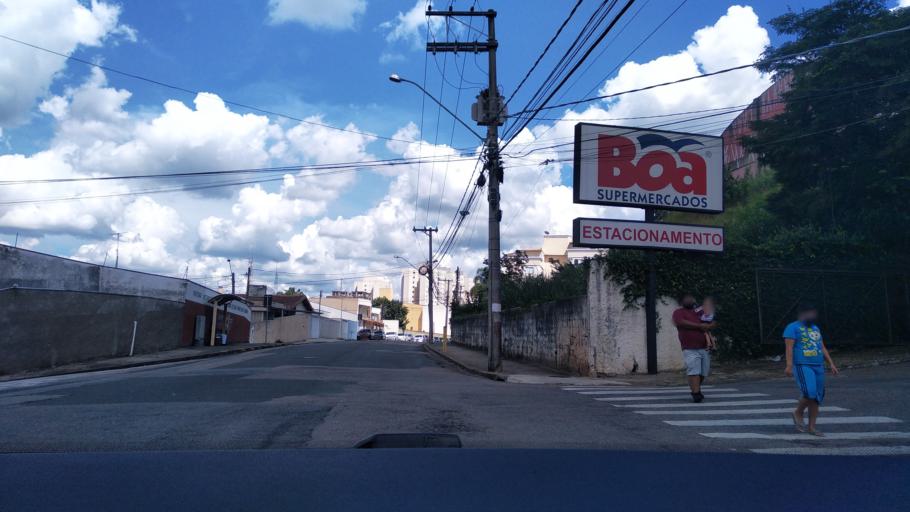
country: BR
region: Sao Paulo
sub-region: Jundiai
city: Jundiai
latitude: -23.2145
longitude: -46.8769
